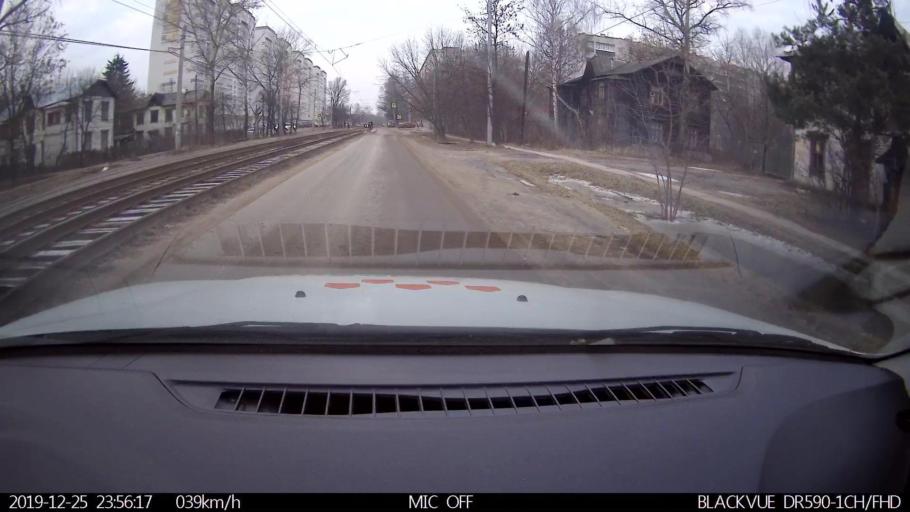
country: RU
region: Nizjnij Novgorod
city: Gorbatovka
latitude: 56.3398
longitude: 43.8403
